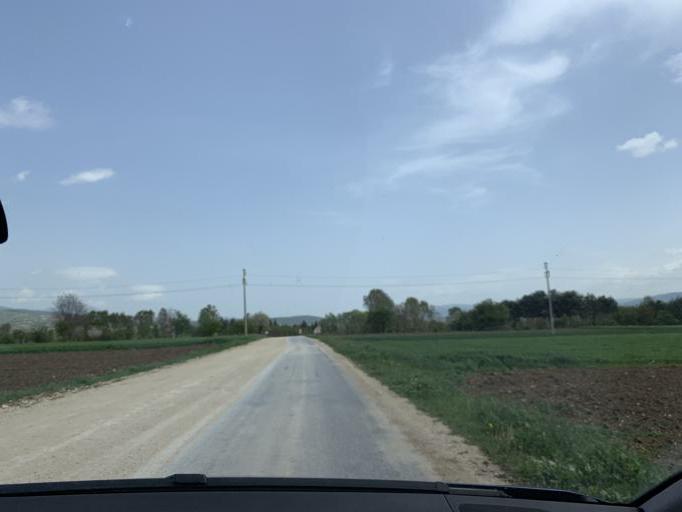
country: TR
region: Bolu
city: Bolu
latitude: 40.7523
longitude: 31.6727
